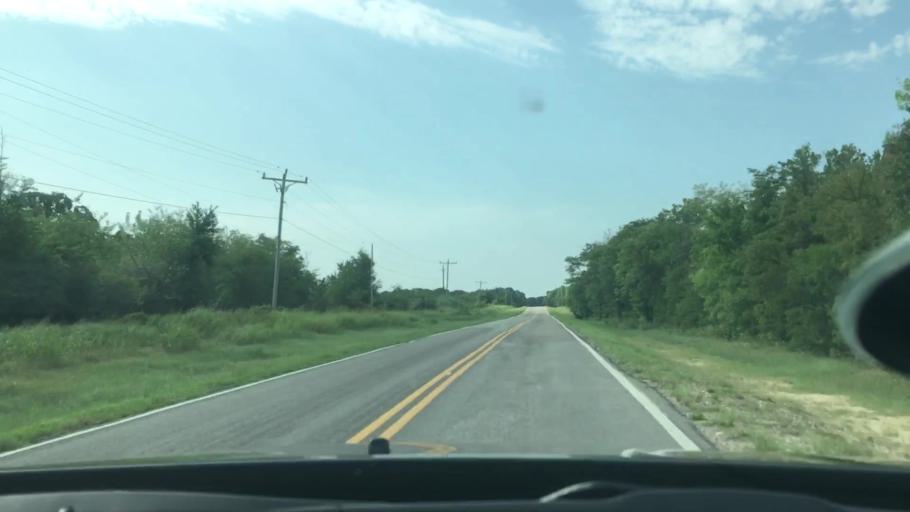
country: US
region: Oklahoma
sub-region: Johnston County
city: Tishomingo
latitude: 34.1785
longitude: -96.5839
